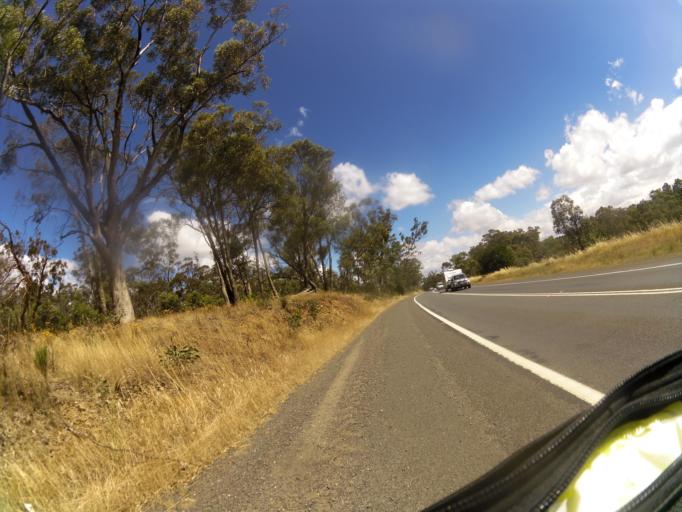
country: AU
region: Victoria
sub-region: Mount Alexander
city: Castlemaine
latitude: -37.0200
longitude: 144.2392
